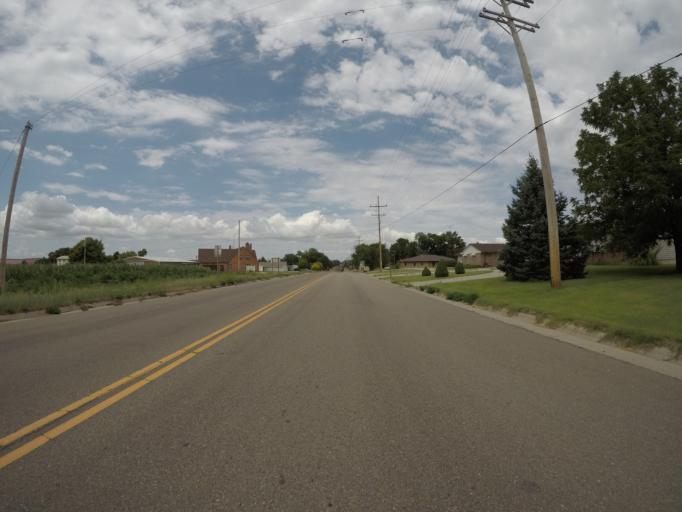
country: US
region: Kansas
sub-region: Rawlins County
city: Atwood
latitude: 39.7983
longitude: -101.0469
